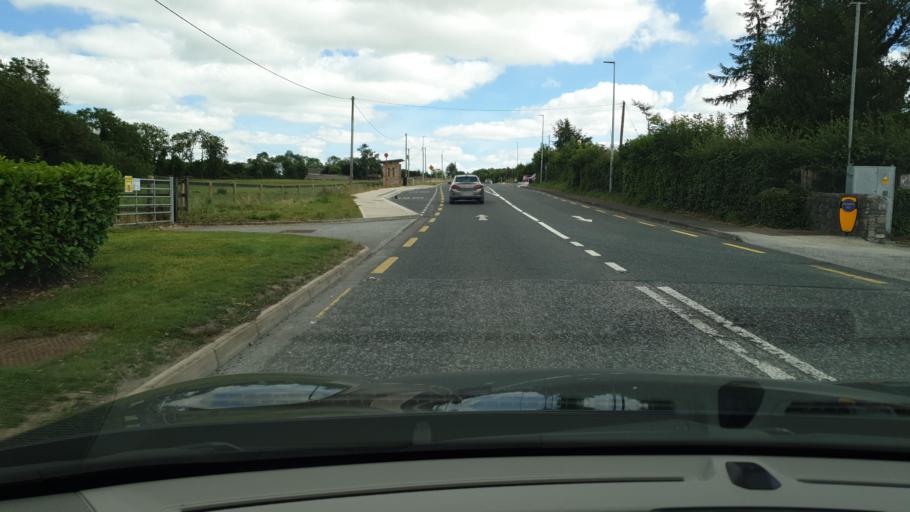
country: IE
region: Leinster
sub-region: An Mhi
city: Newtown Trim
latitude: 53.5260
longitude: -6.6717
